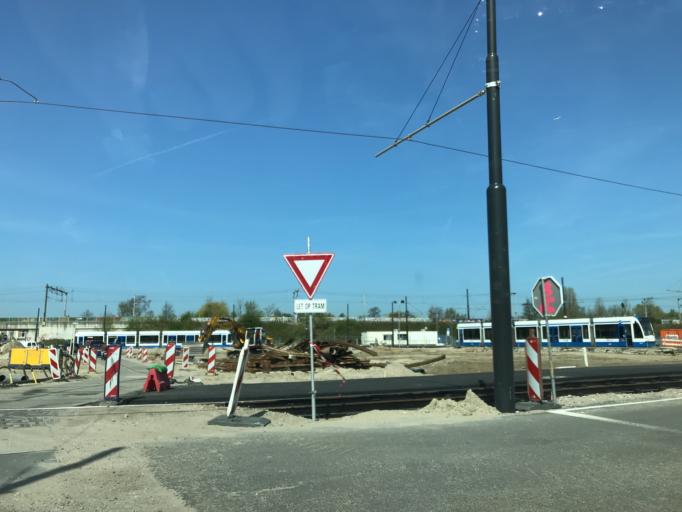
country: NL
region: North Holland
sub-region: Gemeente Diemen
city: Diemen
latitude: 52.3363
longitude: 4.9708
